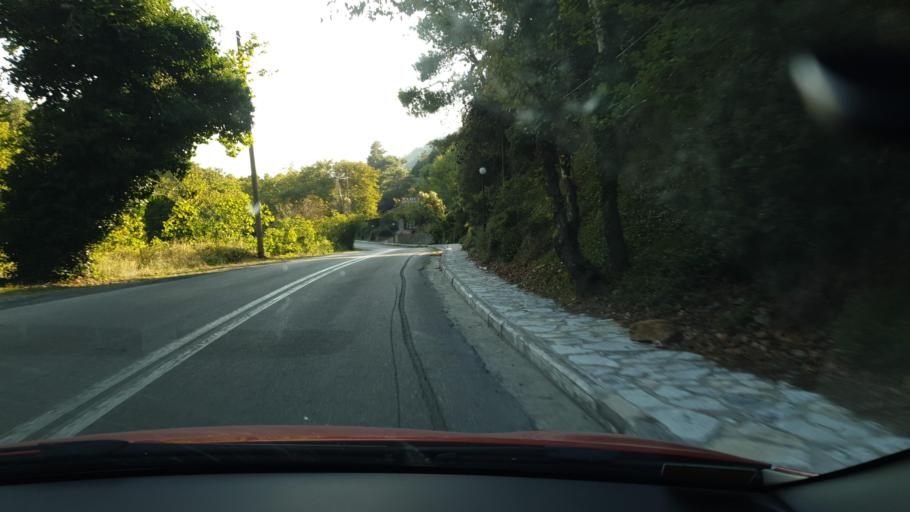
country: GR
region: Central Greece
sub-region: Nomos Evvoias
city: Yimnon
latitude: 38.5850
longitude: 23.8428
